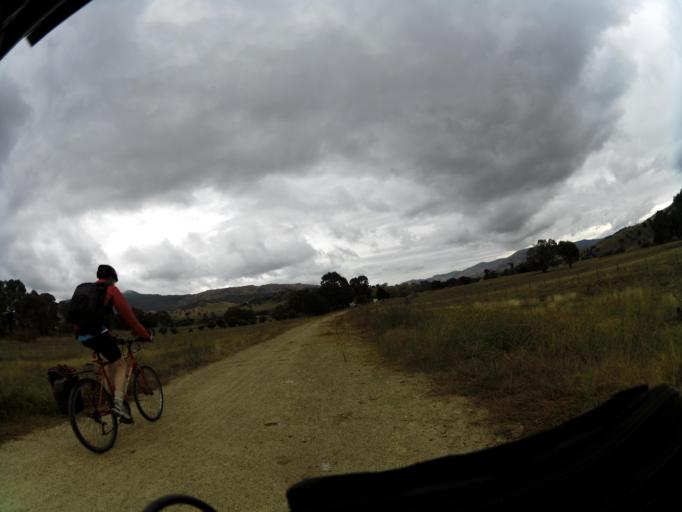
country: AU
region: New South Wales
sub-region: Albury Municipality
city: East Albury
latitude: -36.1922
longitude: 147.3339
